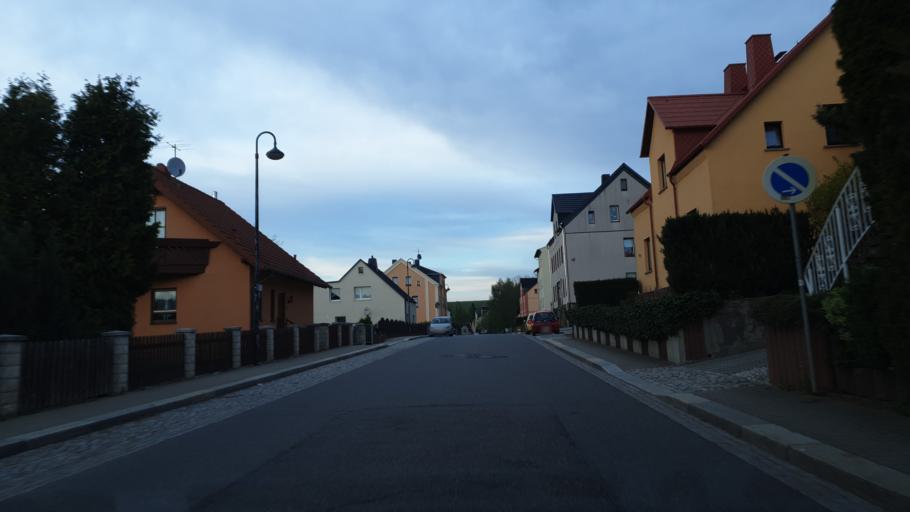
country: DE
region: Saxony
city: Gersdorf
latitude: 50.7432
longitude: 12.7202
